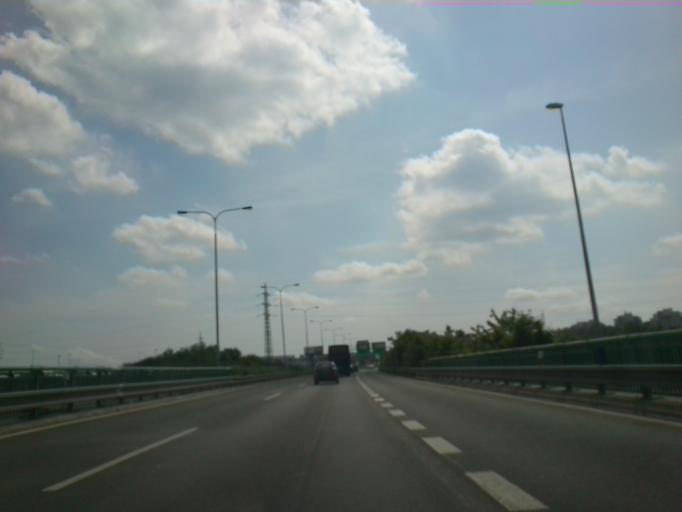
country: CZ
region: Praha
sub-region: Praha 9
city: Strizkov
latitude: 50.1381
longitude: 14.4937
